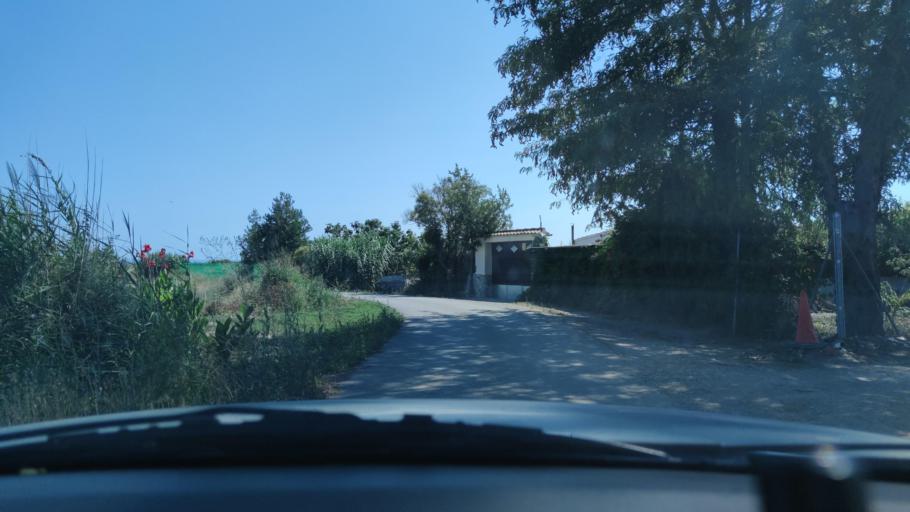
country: ES
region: Catalonia
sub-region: Provincia de Lleida
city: Corbins
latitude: 41.6758
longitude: 0.6610
